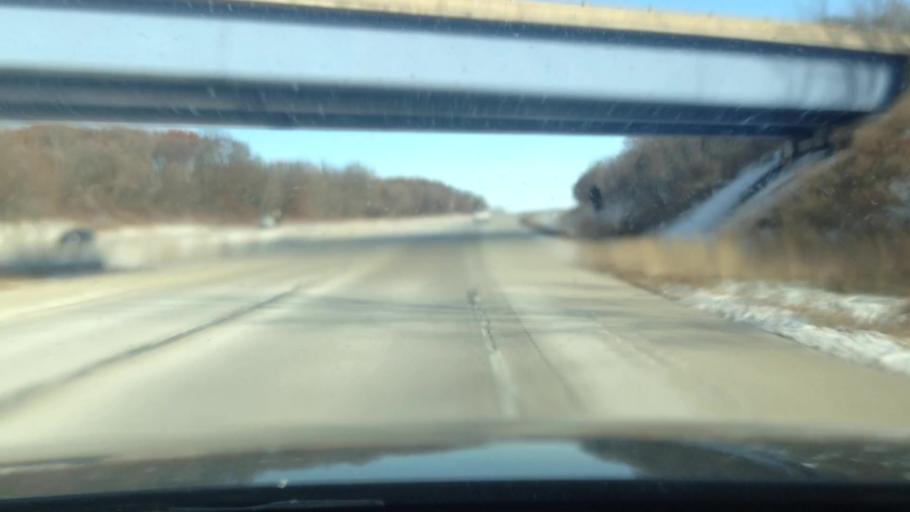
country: US
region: Wisconsin
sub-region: Walworth County
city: Potter Lake
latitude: 42.8266
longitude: -88.3544
